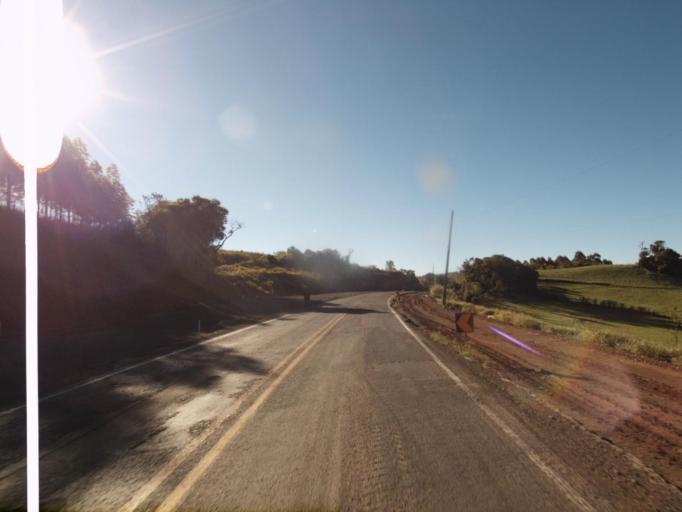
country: AR
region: Misiones
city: Bernardo de Irigoyen
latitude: -26.6350
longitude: -53.5190
